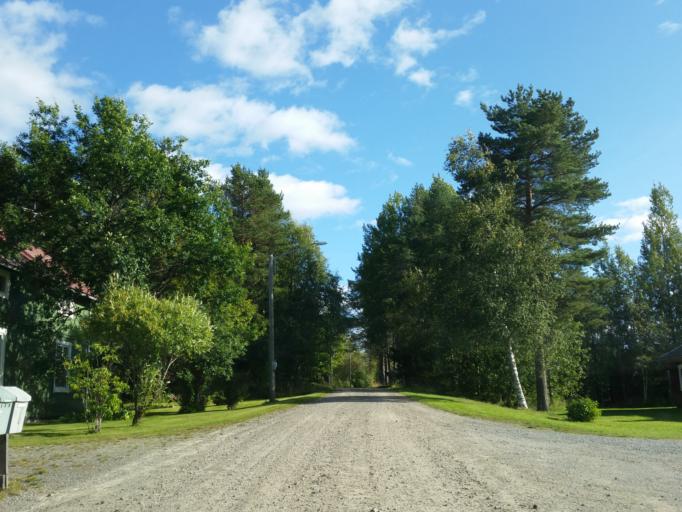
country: SE
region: Vaesterbotten
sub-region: Robertsfors Kommun
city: Robertsfors
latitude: 64.1604
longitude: 20.9566
